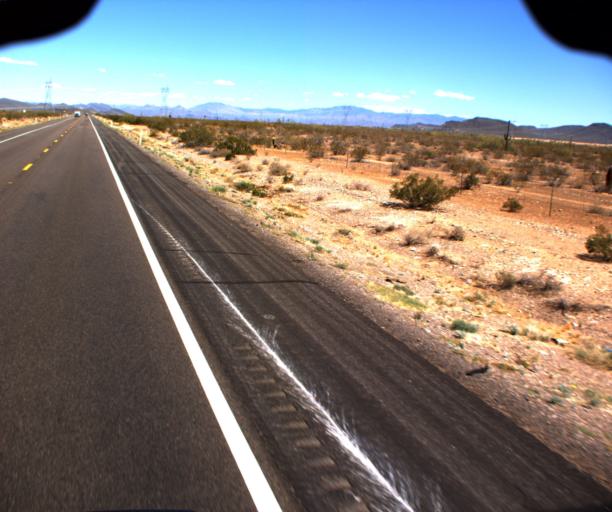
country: US
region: Arizona
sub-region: Maricopa County
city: Anthem
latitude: 33.8147
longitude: -112.2501
